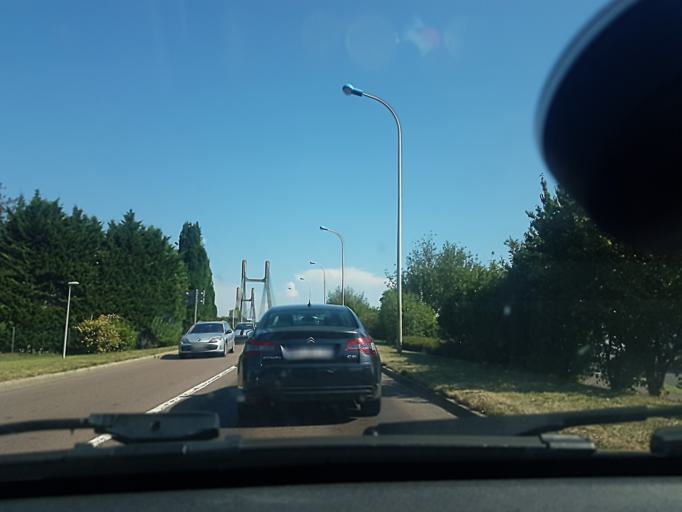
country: FR
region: Bourgogne
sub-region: Departement de Saone-et-Loire
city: Chalon-sur-Saone
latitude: 46.7867
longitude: 4.8669
